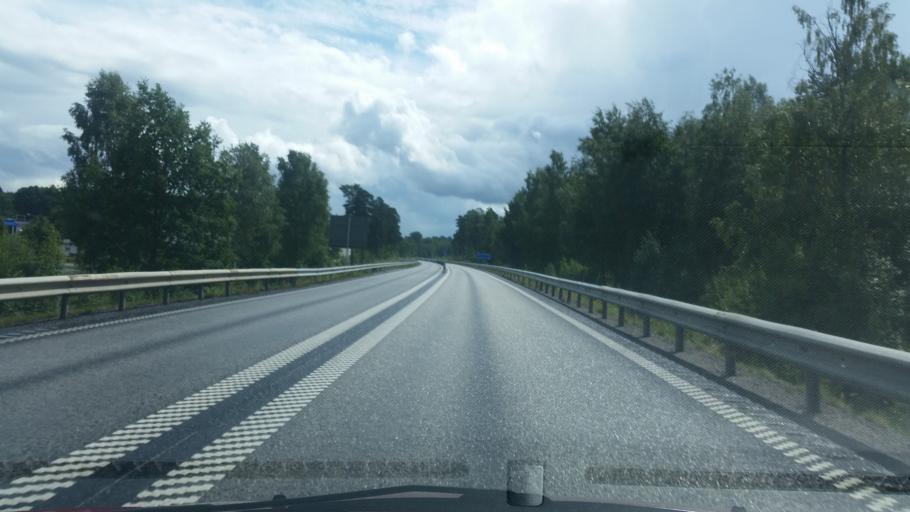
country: SE
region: Joenkoeping
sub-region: Gislaveds Kommun
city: Gislaved
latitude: 57.2724
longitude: 13.6191
